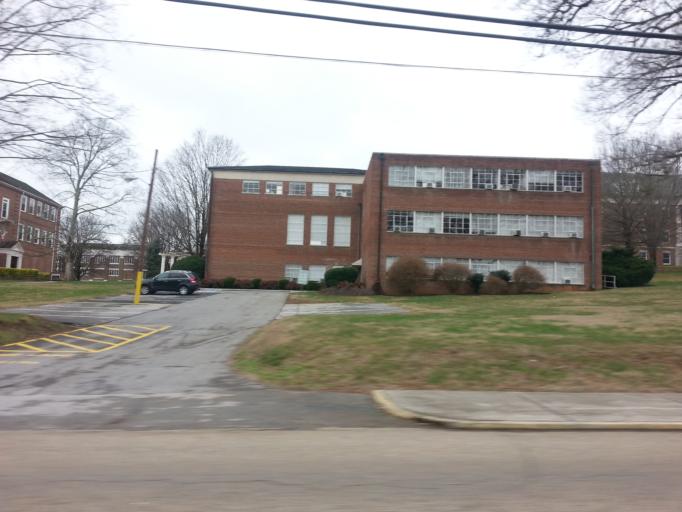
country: US
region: Tennessee
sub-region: Jefferson County
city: Jefferson City
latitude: 36.1219
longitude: -83.4896
